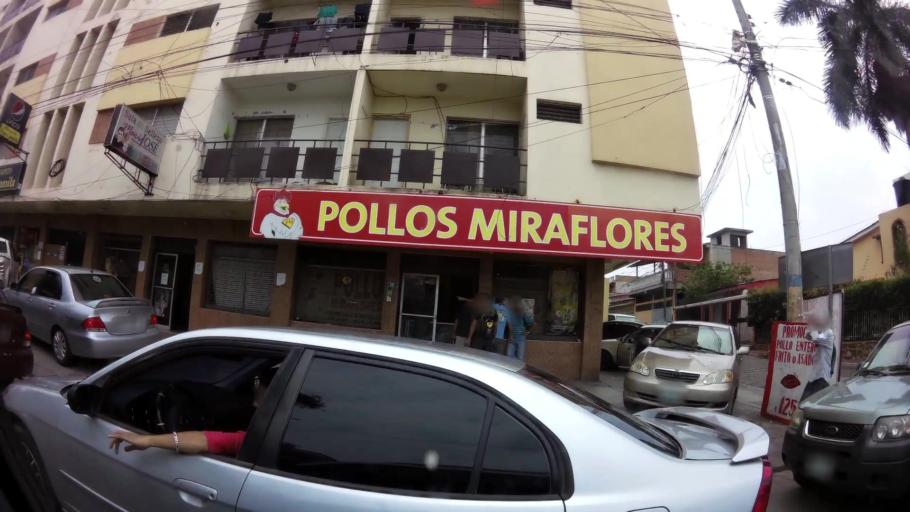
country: HN
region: Francisco Morazan
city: Tegucigalpa
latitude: 14.0728
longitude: -87.1940
